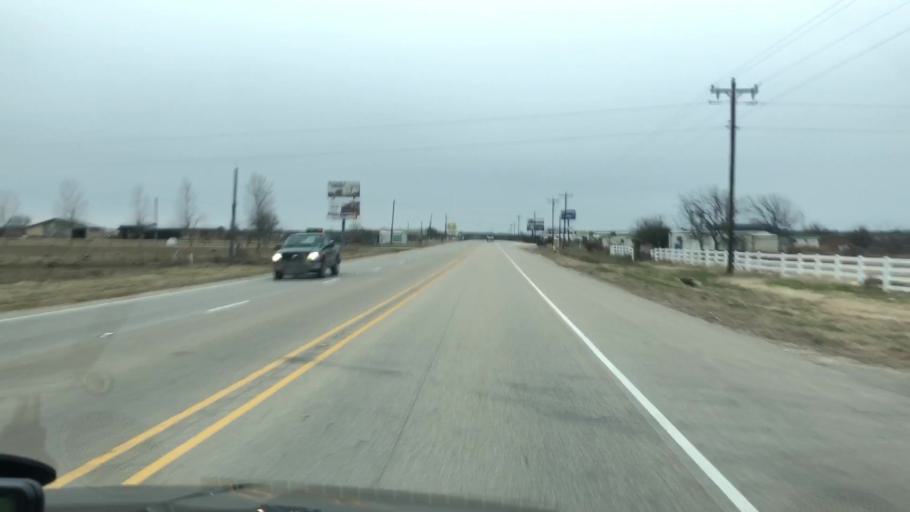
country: US
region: Texas
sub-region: Hamilton County
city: Hamilton
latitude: 31.6748
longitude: -98.1357
